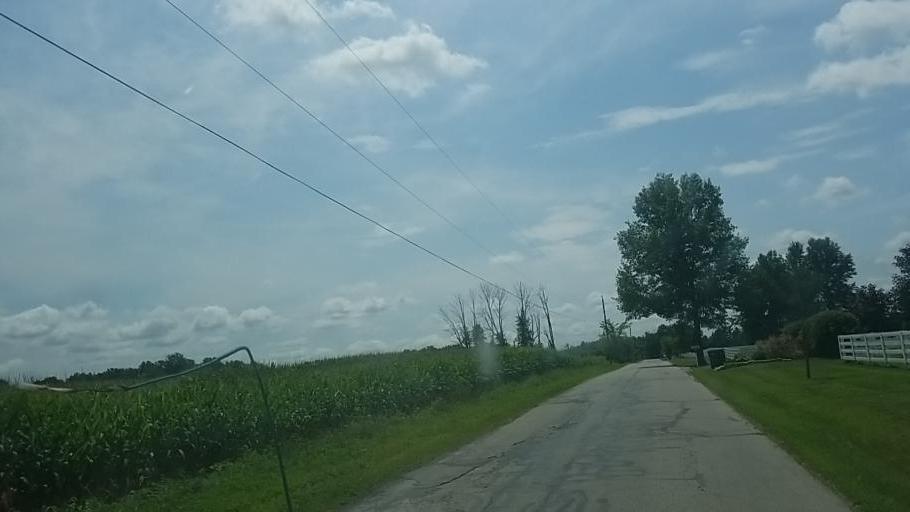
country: US
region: Ohio
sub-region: Franklin County
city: New Albany
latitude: 40.0224
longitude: -82.7699
